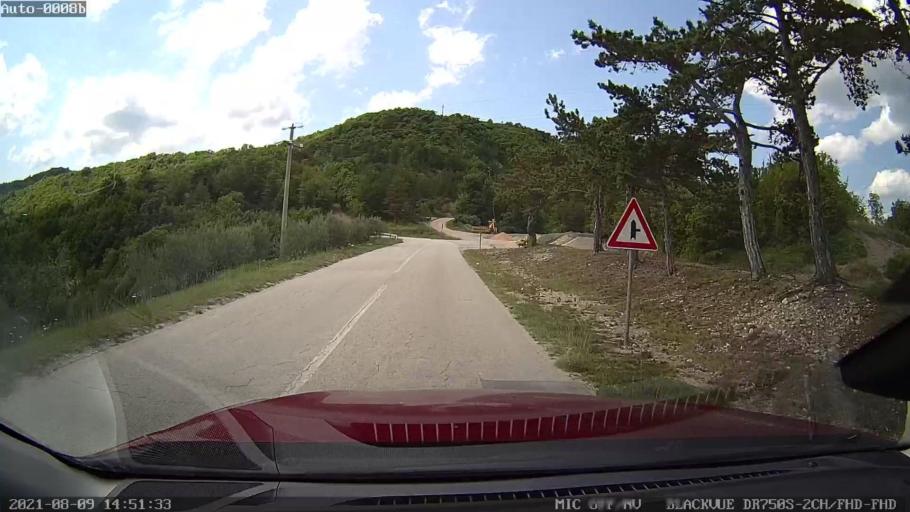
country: HR
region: Istarska
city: Pazin
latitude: 45.2915
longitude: 14.0895
